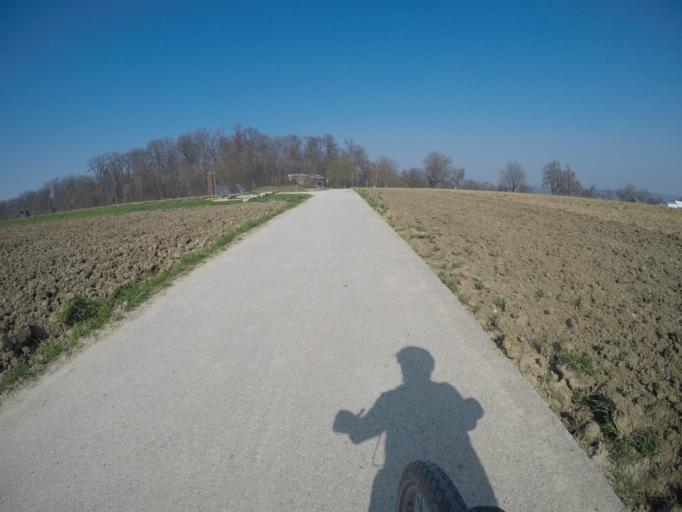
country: DE
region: Baden-Wuerttemberg
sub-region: Regierungsbezirk Stuttgart
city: Altdorf
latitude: 48.5915
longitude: 9.2647
